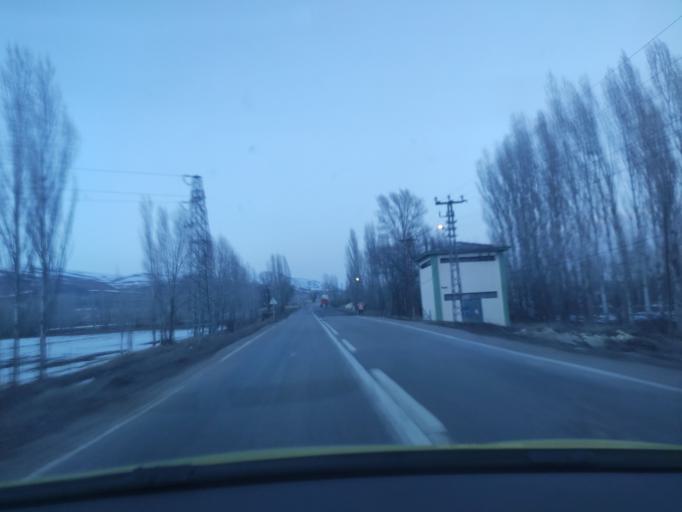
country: TR
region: Bayburt
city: Aydintepe
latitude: 40.3716
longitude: 40.1114
